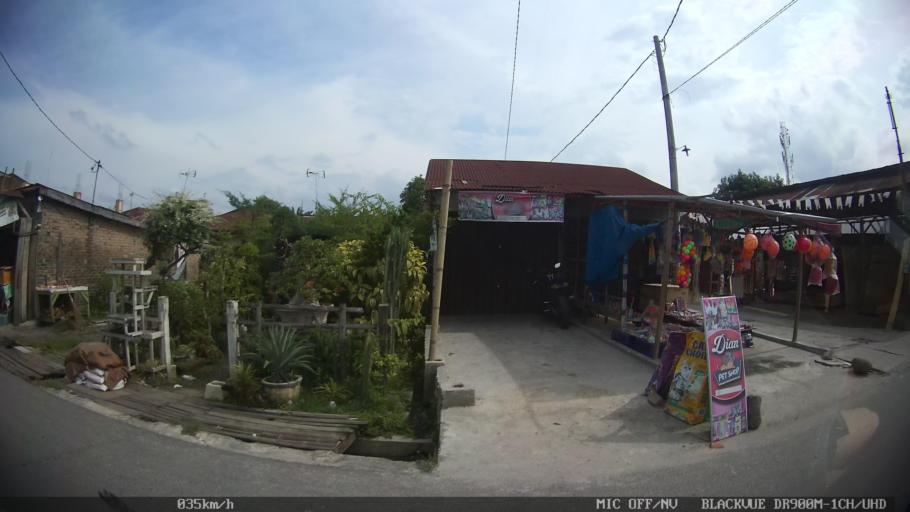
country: ID
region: North Sumatra
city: Percut
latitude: 3.6071
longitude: 98.7708
